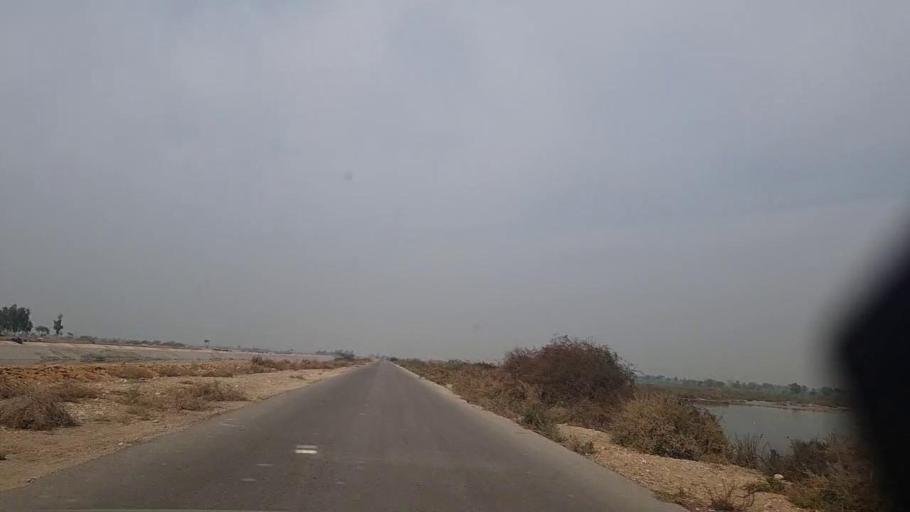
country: PK
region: Sindh
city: Sakrand
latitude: 26.2706
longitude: 68.2354
